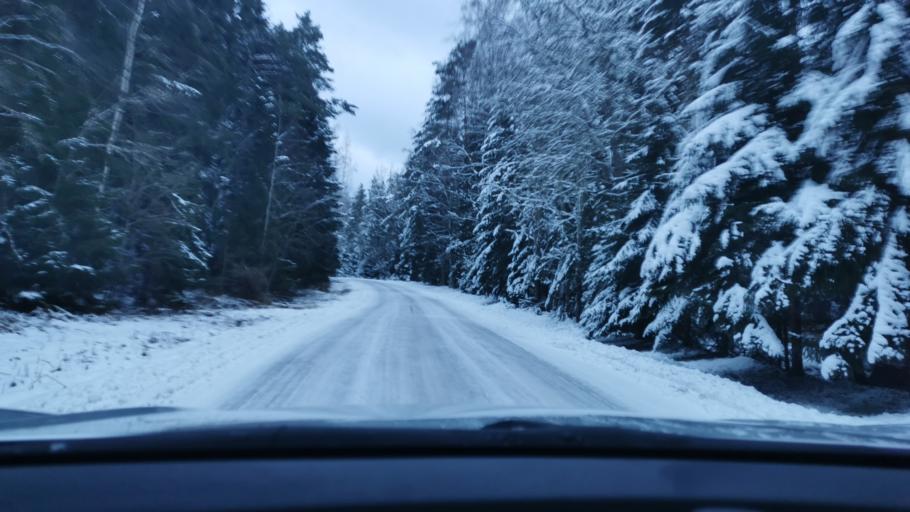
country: EE
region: Laeaene-Virumaa
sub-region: Haljala vald
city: Haljala
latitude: 59.5604
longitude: 26.3138
